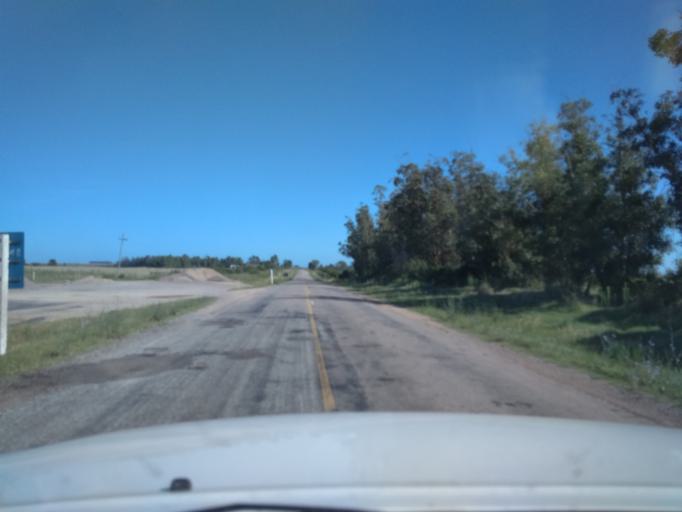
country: UY
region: Canelones
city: San Ramon
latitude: -34.2029
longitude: -55.9332
